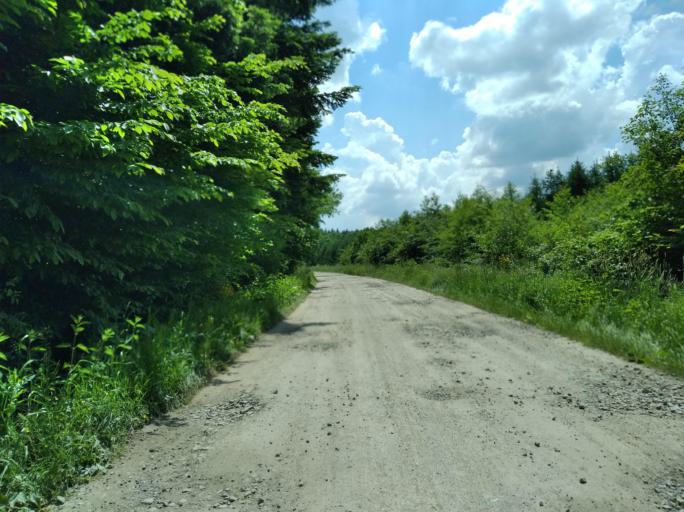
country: PL
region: Subcarpathian Voivodeship
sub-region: Powiat ropczycko-sedziszowski
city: Zagorzyce
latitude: 49.9722
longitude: 21.6873
